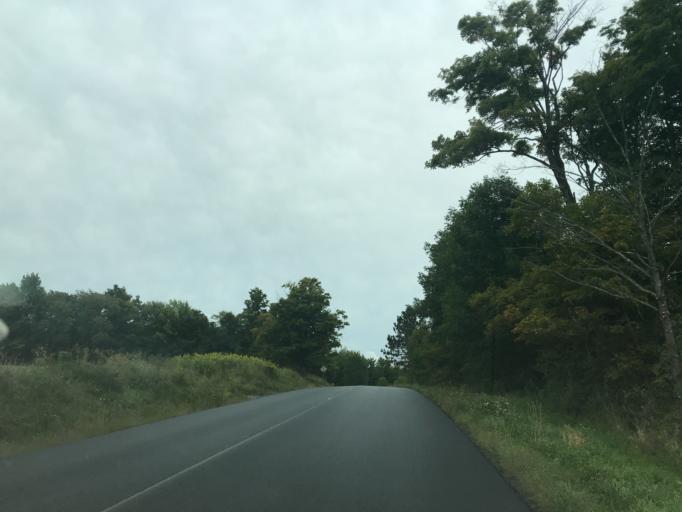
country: US
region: New York
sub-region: Delaware County
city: Stamford
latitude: 42.5198
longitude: -74.6238
